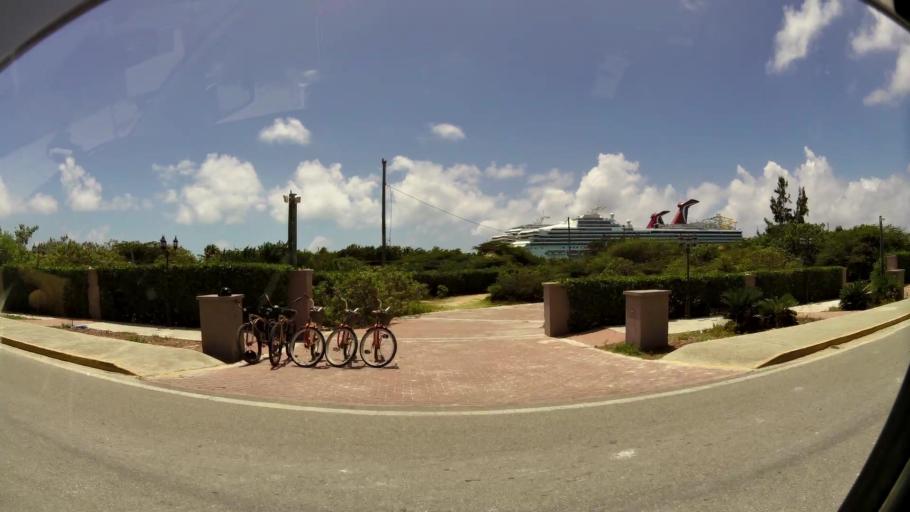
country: TC
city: Cockburn Town
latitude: 21.4298
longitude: -71.1440
